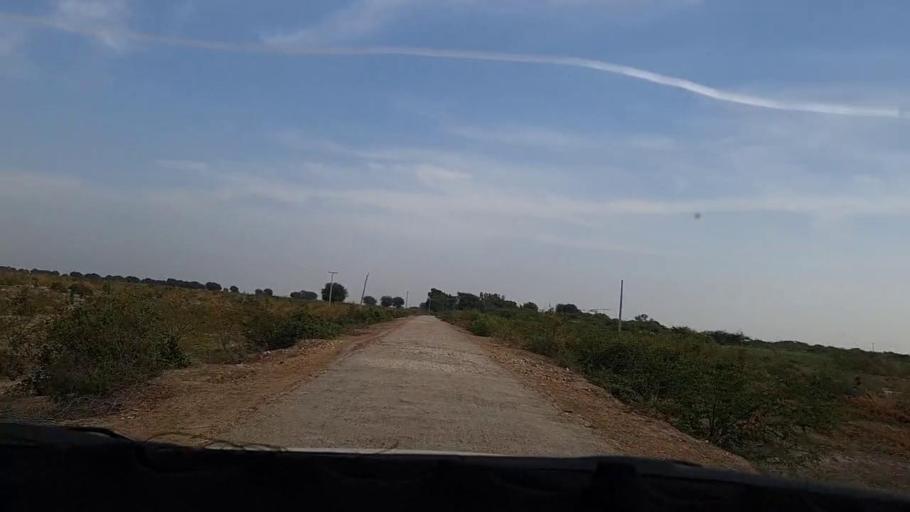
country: PK
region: Sindh
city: Pithoro
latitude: 25.5365
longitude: 69.3372
